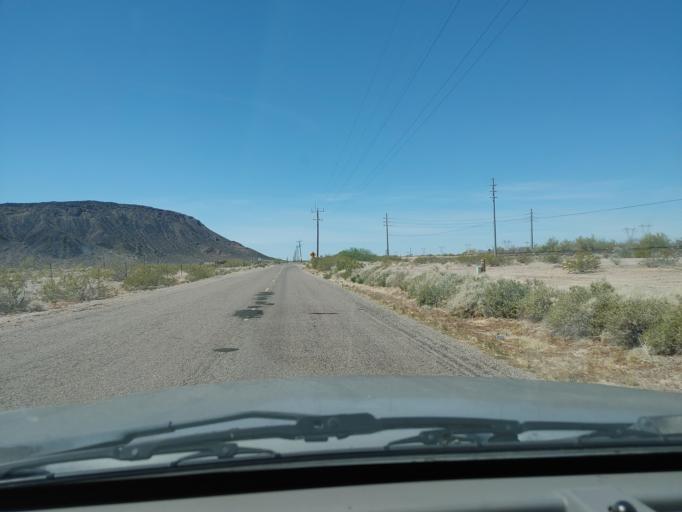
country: US
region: Arizona
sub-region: Maricopa County
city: Gila Bend
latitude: 33.0216
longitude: -113.3381
